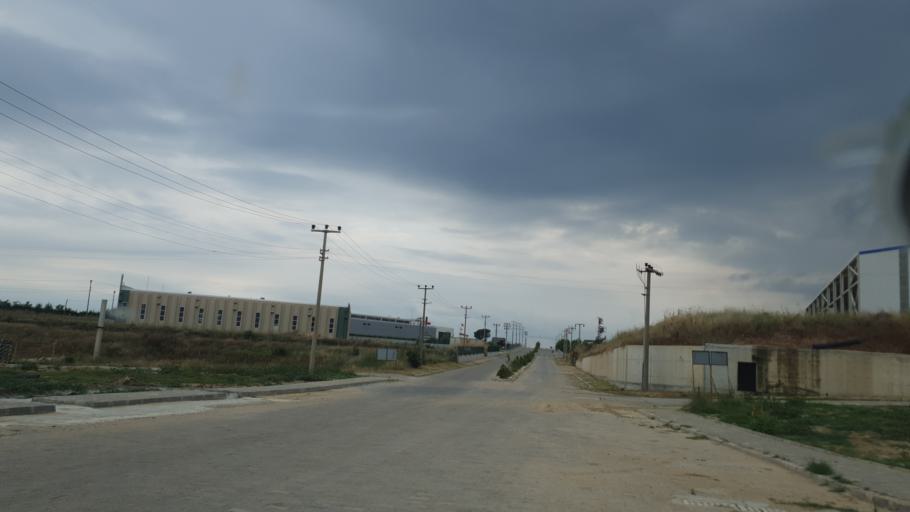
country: TR
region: Tekirdag
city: Hayrabolu
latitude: 41.2260
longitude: 27.0476
